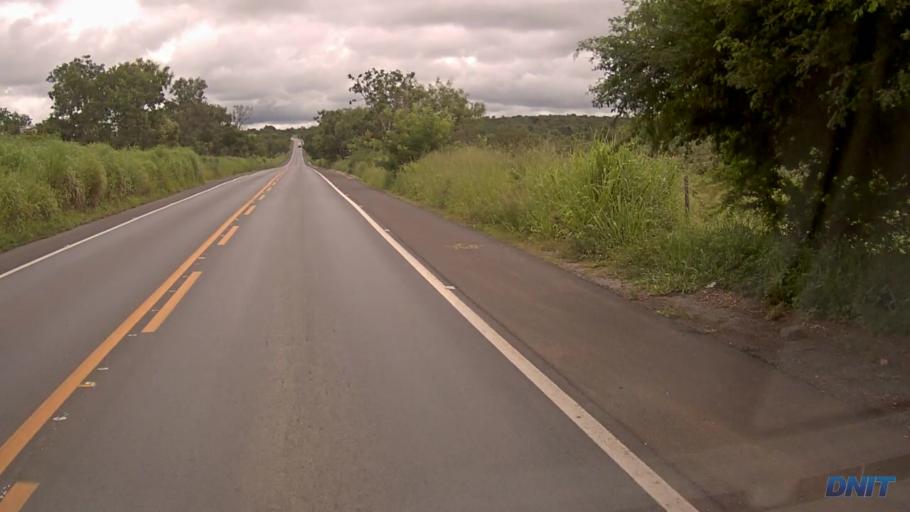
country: BR
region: Goias
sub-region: Posse
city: Posse
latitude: -14.2793
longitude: -46.4058
